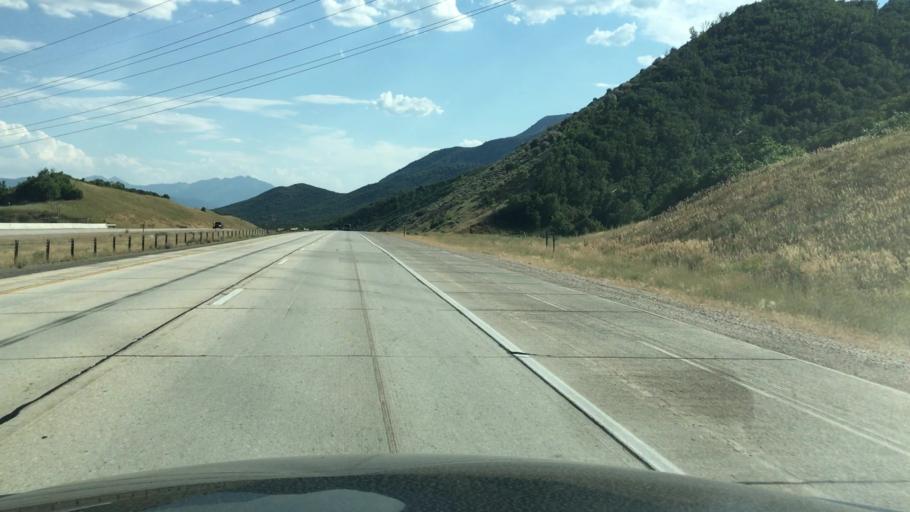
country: US
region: Utah
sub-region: Summit County
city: Park City
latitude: 40.6009
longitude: -111.4318
